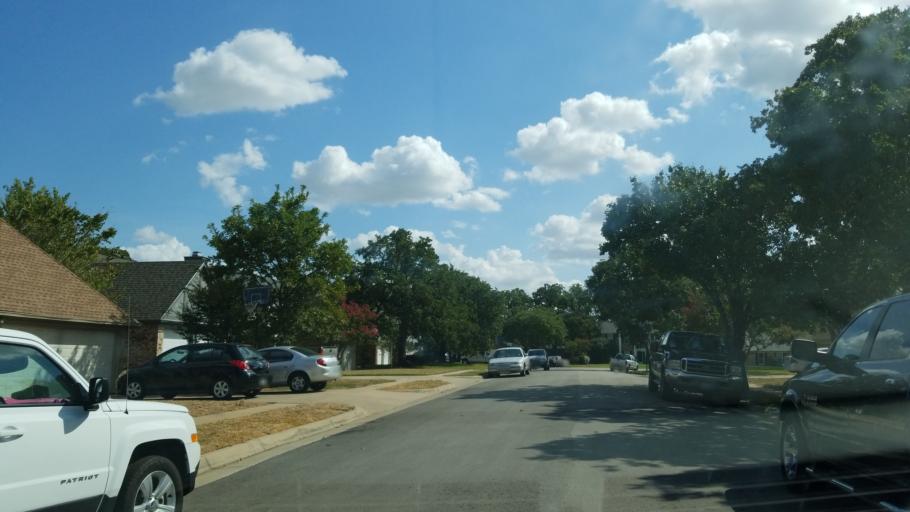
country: US
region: Texas
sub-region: Tarrant County
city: Euless
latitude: 32.8621
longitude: -97.0786
